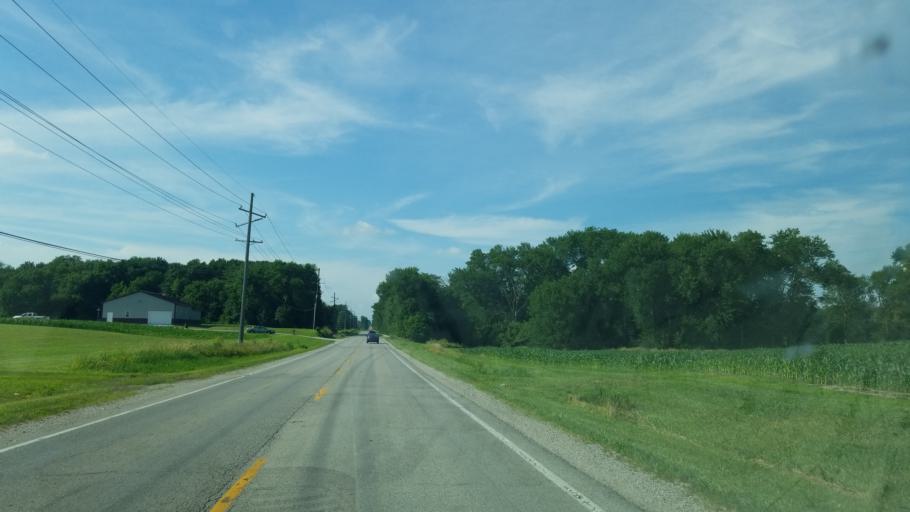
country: US
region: Illinois
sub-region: Saint Clair County
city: Lebanon
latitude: 38.5730
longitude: -89.8078
